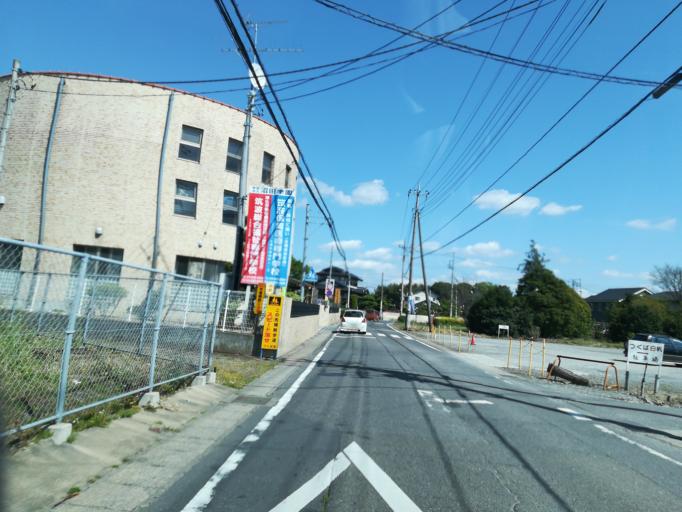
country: JP
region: Ibaraki
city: Naka
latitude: 36.0754
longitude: 140.1070
